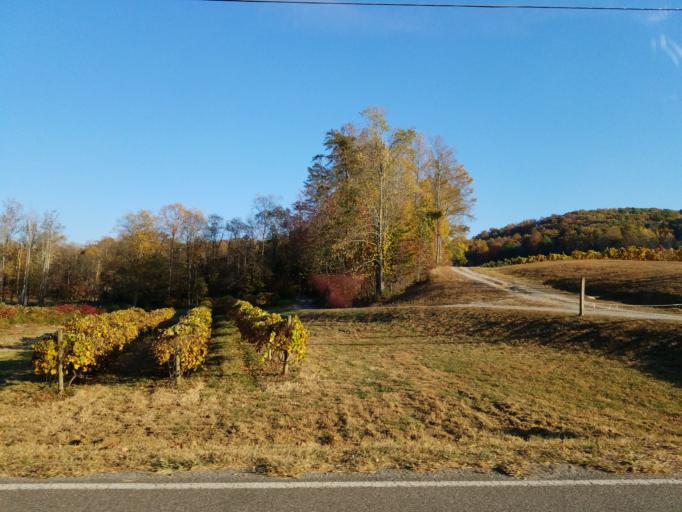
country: US
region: Georgia
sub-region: Gilmer County
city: Ellijay
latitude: 34.6158
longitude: -84.3916
